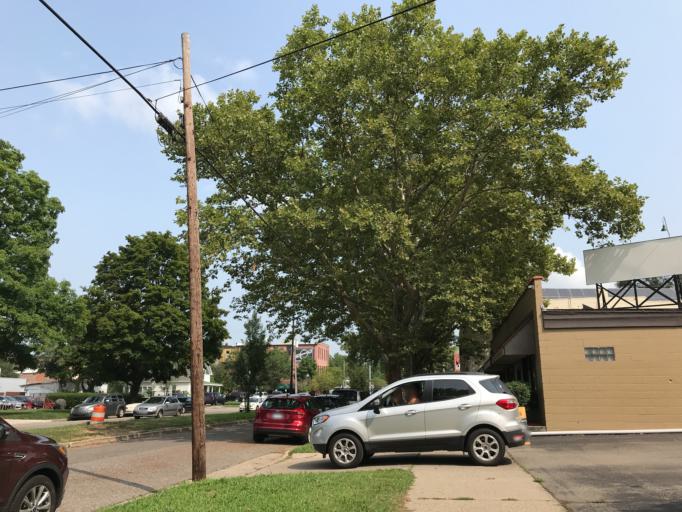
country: US
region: Michigan
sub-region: Washtenaw County
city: Ypsilanti
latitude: 42.2445
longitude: -83.6084
